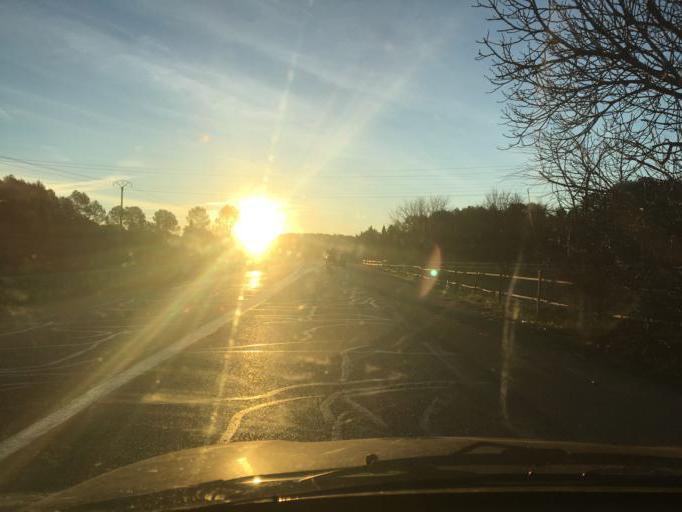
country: FR
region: Provence-Alpes-Cote d'Azur
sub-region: Departement du Var
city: Lorgues
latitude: 43.4682
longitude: 6.3851
